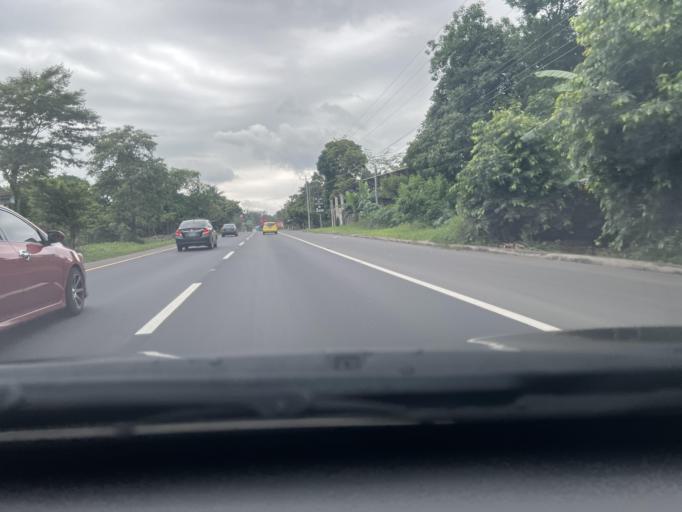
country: SV
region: Santa Ana
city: El Congo
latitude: 13.8819
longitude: -89.4931
